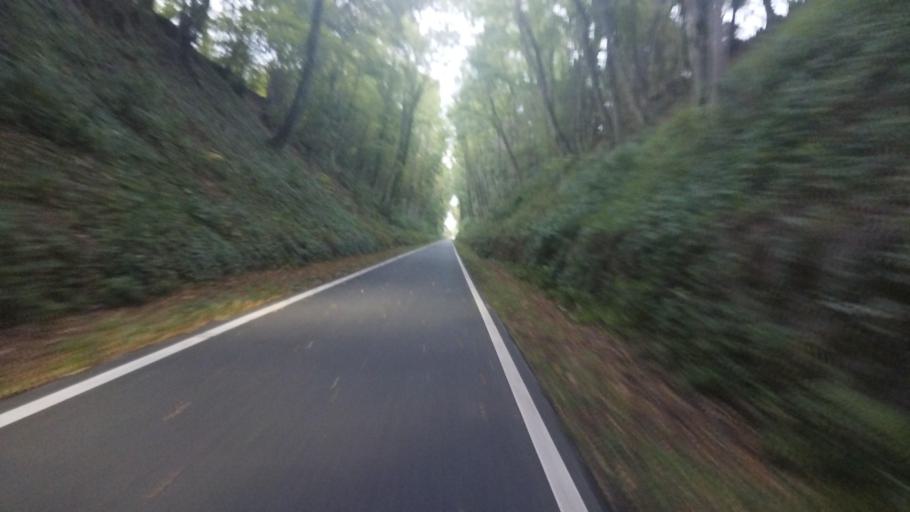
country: DE
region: North Rhine-Westphalia
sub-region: Regierungsbezirk Munster
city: Horstmar
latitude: 52.0578
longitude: 7.3204
